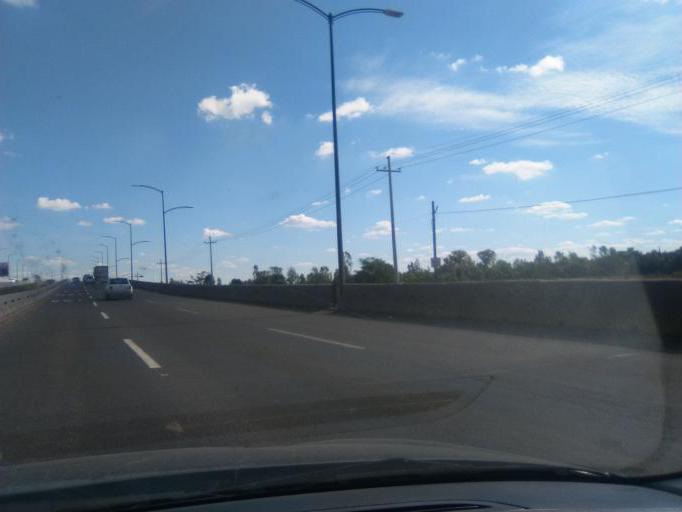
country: MX
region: Guanajuato
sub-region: Leon
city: Ladrilleras del Refugio
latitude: 21.0655
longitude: -101.5899
